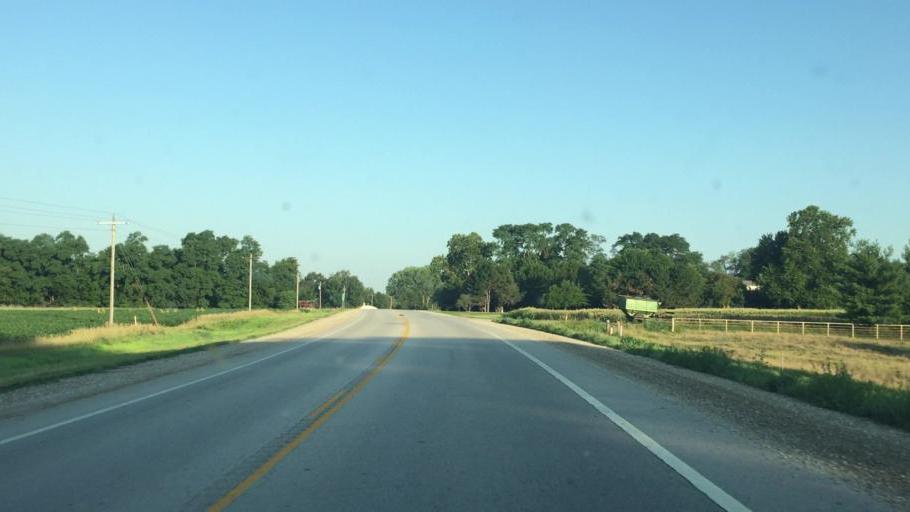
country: US
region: Kansas
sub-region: Doniphan County
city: Wathena
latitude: 39.7755
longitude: -94.9657
